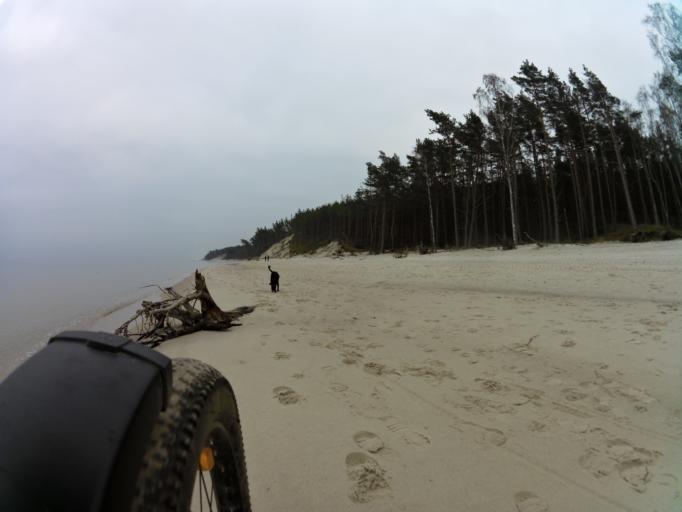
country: PL
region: Pomeranian Voivodeship
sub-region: Powiat pucki
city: Krokowa
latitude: 54.8318
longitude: 18.1317
